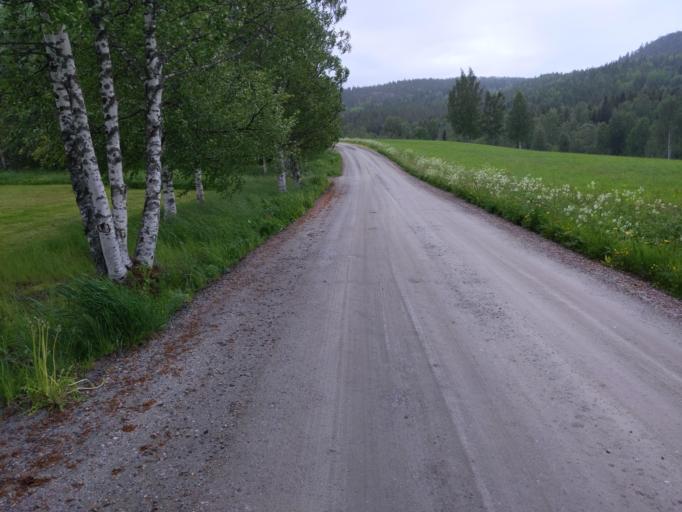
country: SE
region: Vaesternorrland
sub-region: OErnskoeldsviks Kommun
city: Ornskoldsvik
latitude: 63.2139
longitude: 18.6891
